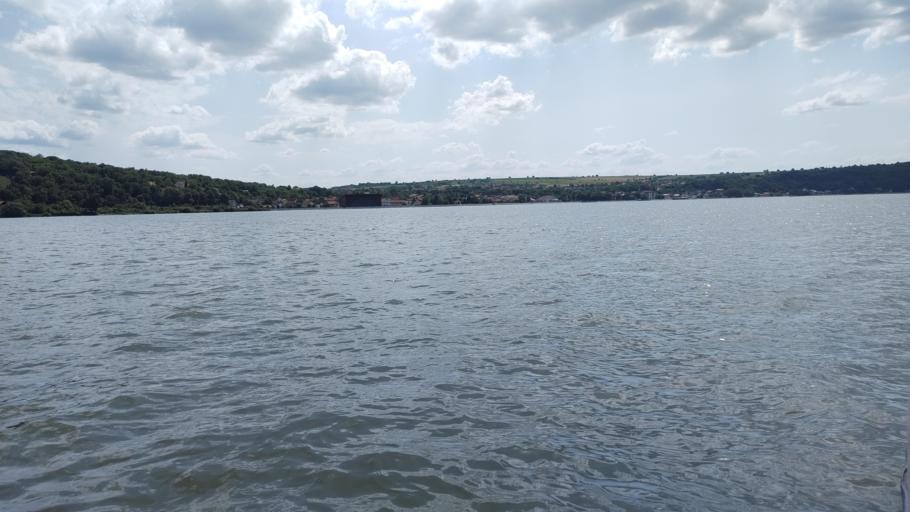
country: RS
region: Central Serbia
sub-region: Branicevski Okrug
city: Golubac
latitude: 44.6586
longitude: 21.6447
